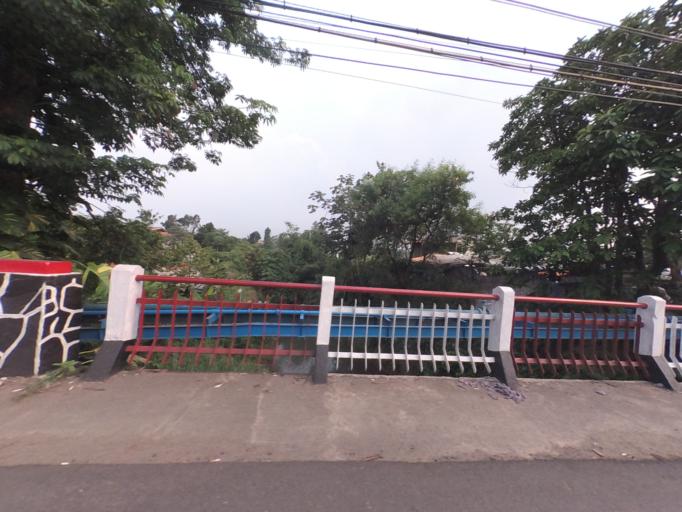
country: ID
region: West Java
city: Ciampea
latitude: -6.5689
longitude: 106.6692
